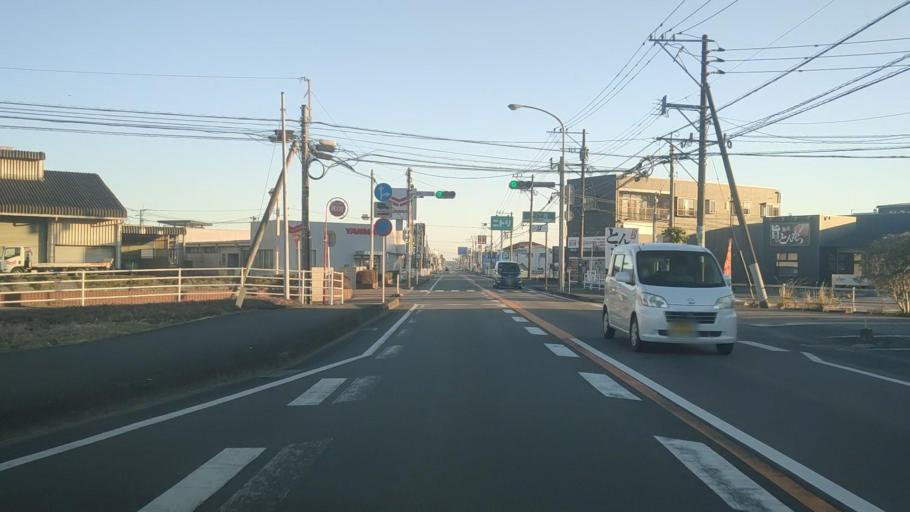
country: JP
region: Miyazaki
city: Miyazaki-shi
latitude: 31.9764
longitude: 131.4428
